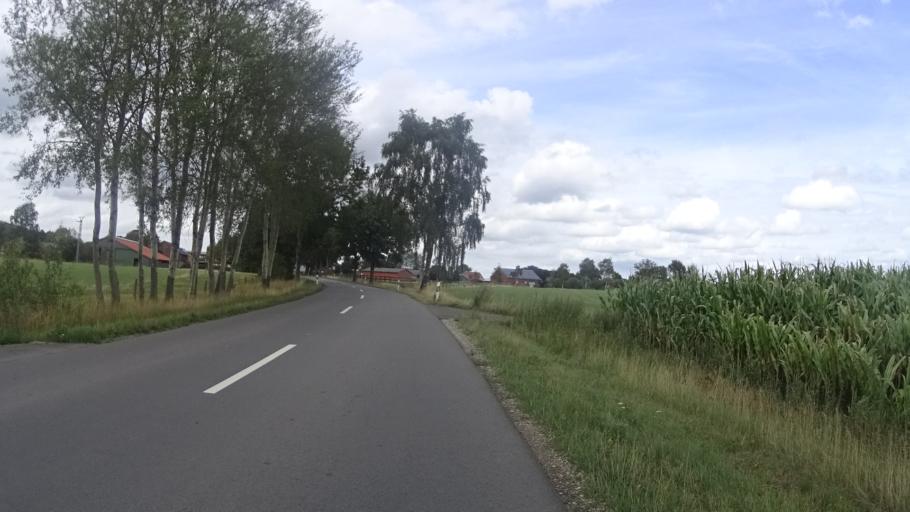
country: DE
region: Lower Saxony
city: Mittelstenahe
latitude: 53.6612
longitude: 9.0416
